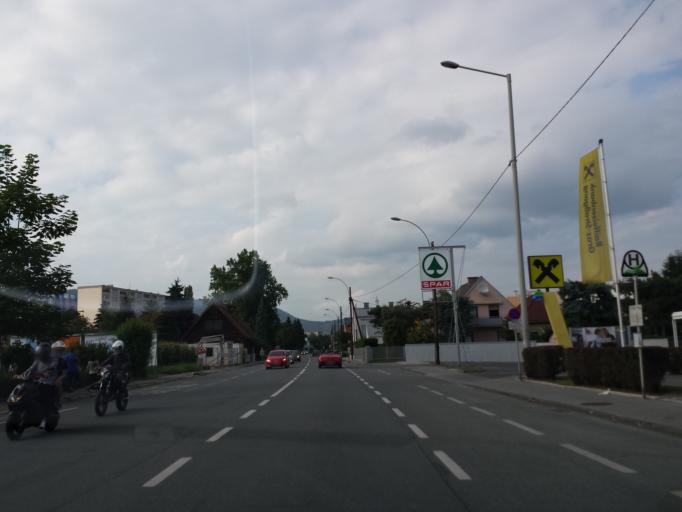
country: AT
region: Styria
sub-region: Graz Stadt
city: Wetzelsdorf
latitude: 47.0473
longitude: 15.3949
